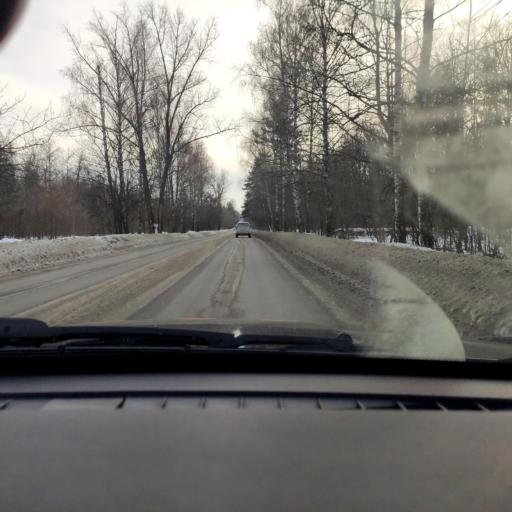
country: RU
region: Samara
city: Pribrezhnyy
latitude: 53.5117
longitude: 49.8507
